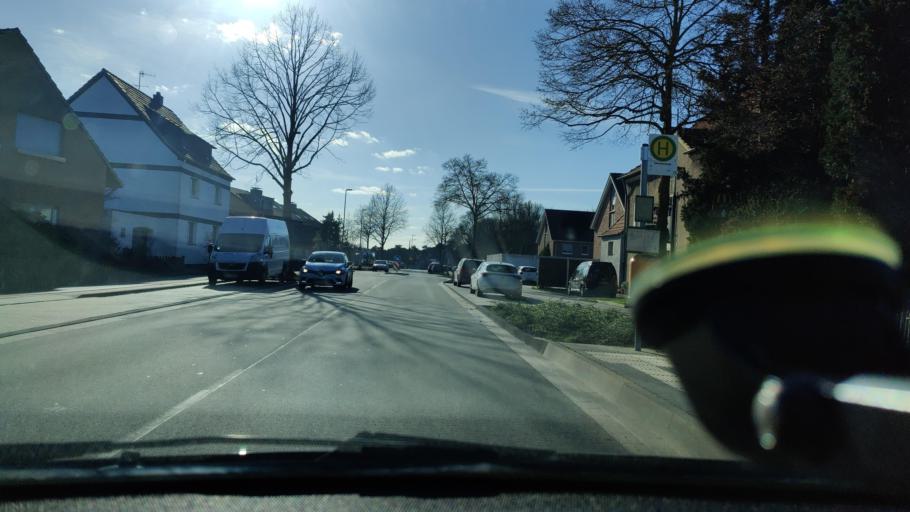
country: DE
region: North Rhine-Westphalia
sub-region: Regierungsbezirk Dusseldorf
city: Dinslaken
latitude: 51.5809
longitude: 6.7729
